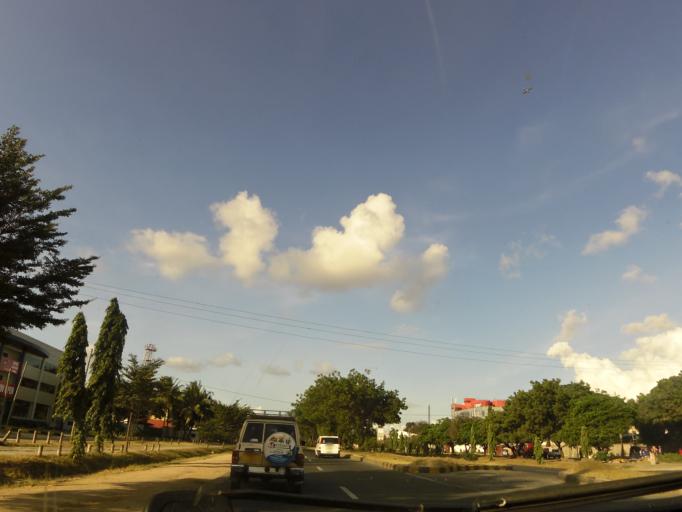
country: TZ
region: Dar es Salaam
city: Dar es Salaam
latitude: -6.8368
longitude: 39.2601
